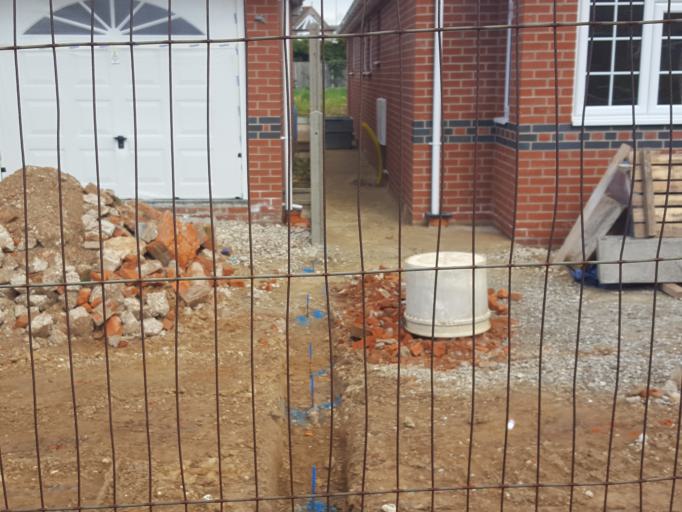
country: GB
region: England
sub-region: Essex
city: Clacton-on-Sea
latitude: 51.7921
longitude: 1.1624
